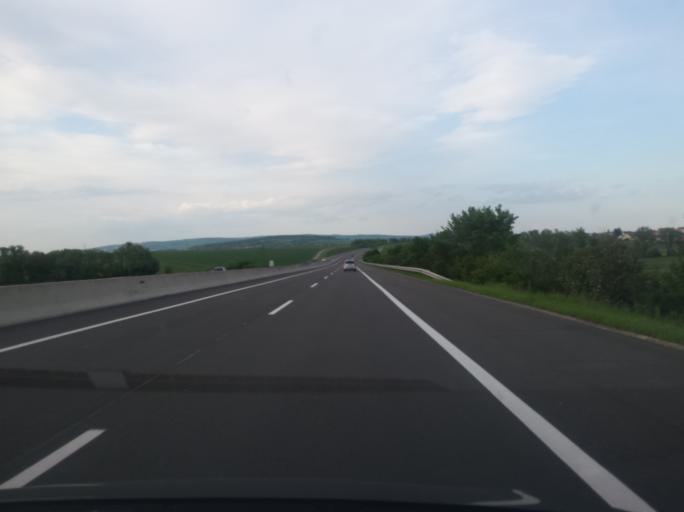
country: AT
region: Burgenland
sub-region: Politischer Bezirk Mattersburg
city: Hirm
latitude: 47.7851
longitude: 16.4400
